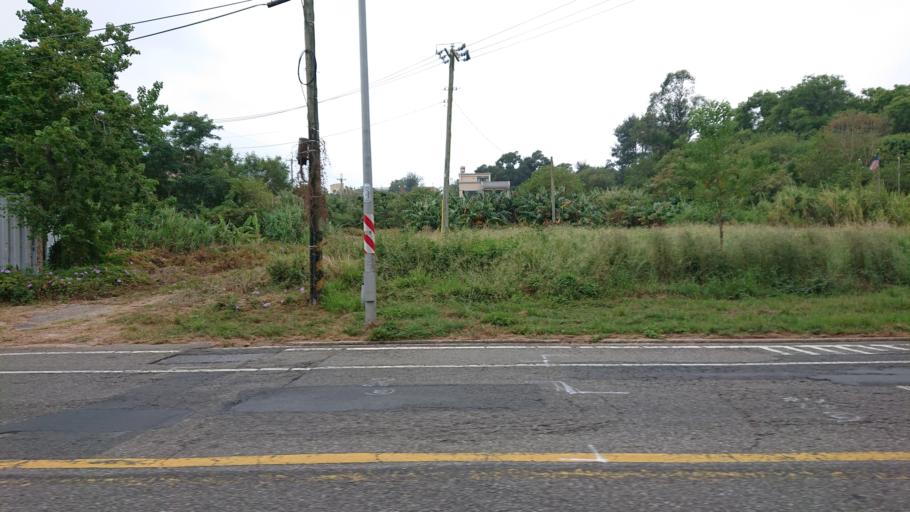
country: TW
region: Fukien
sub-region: Kinmen
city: Jincheng
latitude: 24.4423
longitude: 118.3899
